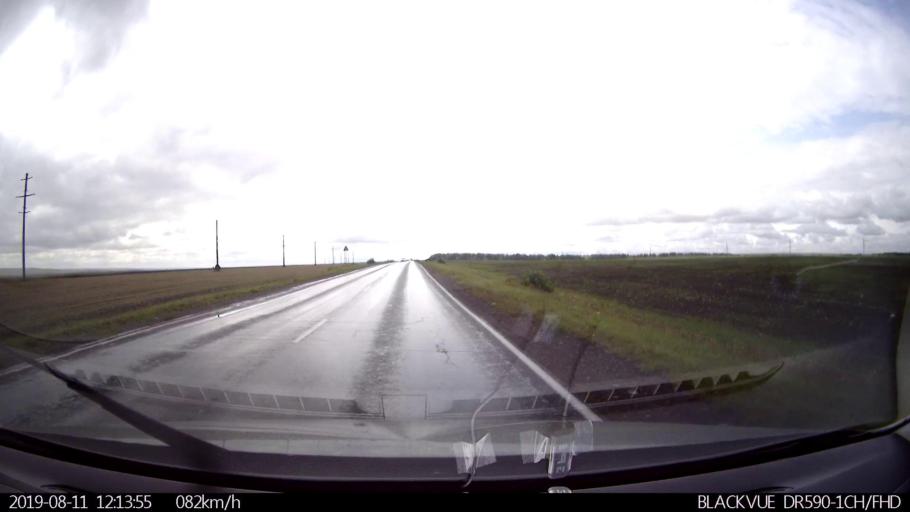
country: RU
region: Ulyanovsk
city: Ignatovka
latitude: 53.9572
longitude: 47.9869
